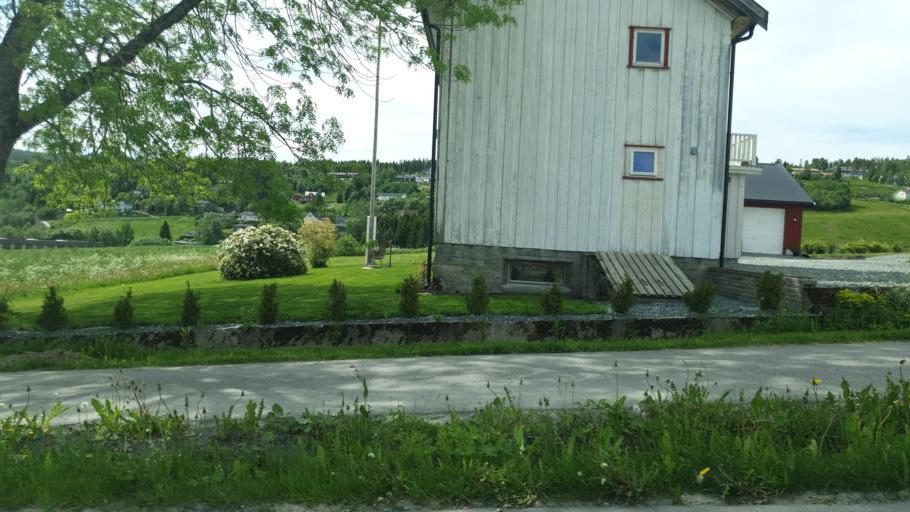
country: NO
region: Nord-Trondelag
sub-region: Leksvik
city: Leksvik
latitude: 63.6700
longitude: 10.6113
